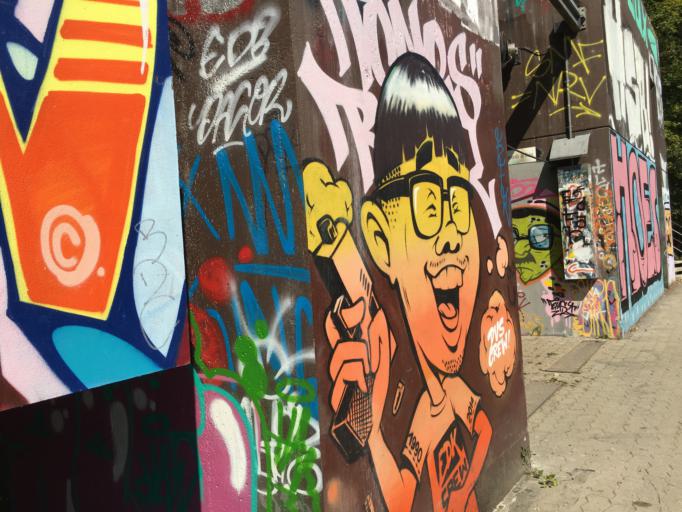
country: CH
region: Geneva
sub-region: Geneva
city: Lancy
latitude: 46.2017
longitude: 6.1215
